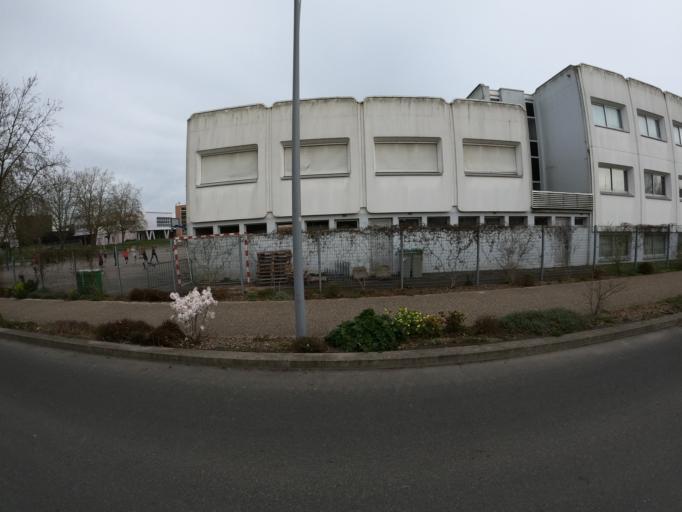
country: FR
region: Pays de la Loire
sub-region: Departement de la Vendee
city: Montaigu
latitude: 46.9820
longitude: -1.3092
